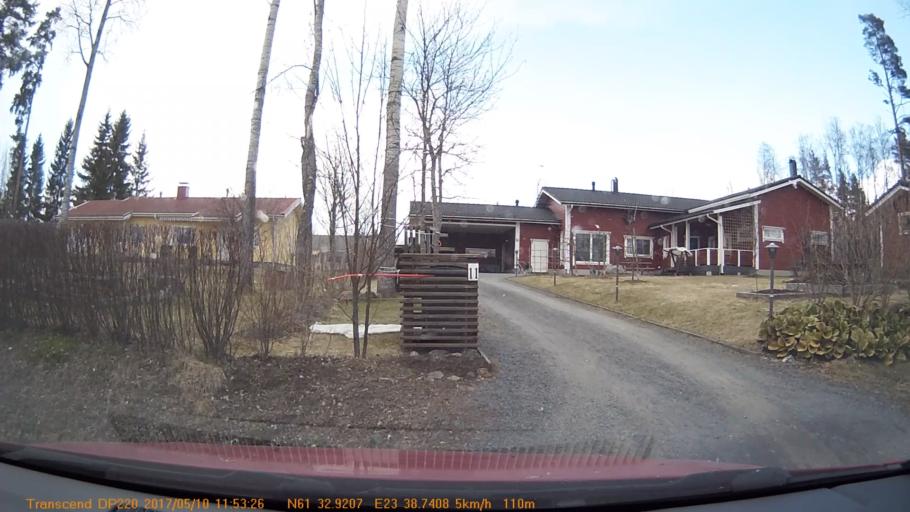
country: FI
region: Pirkanmaa
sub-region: Tampere
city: Yloejaervi
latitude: 61.5487
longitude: 23.6454
